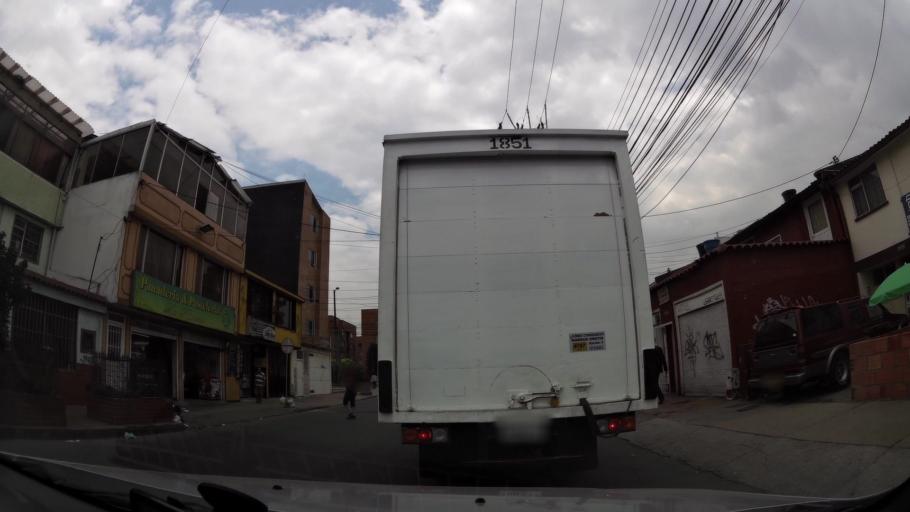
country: CO
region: Bogota D.C.
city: Bogota
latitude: 4.5960
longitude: -74.1096
